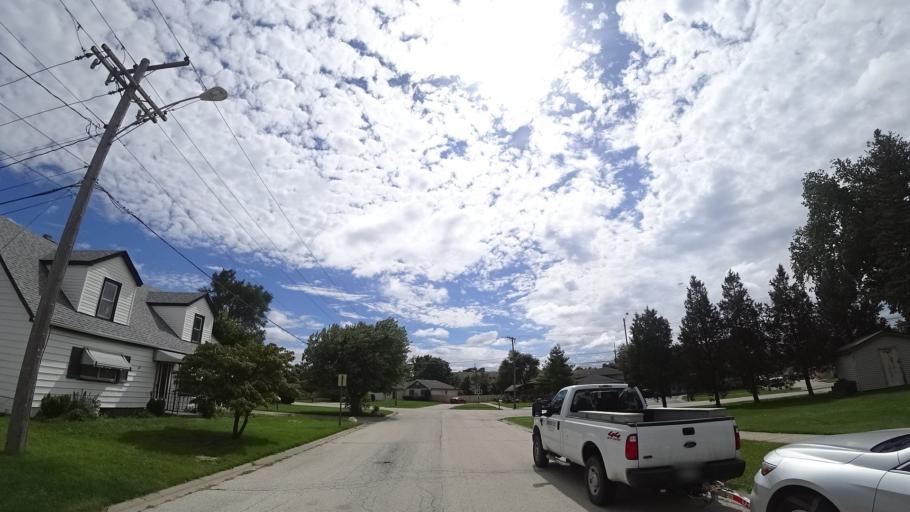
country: US
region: Illinois
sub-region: Cook County
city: Chicago Ridge
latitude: 41.7171
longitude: -87.7963
